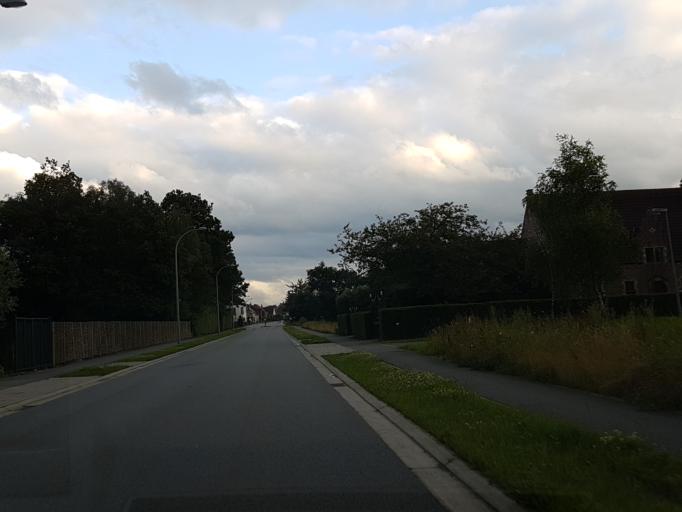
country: BE
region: Flanders
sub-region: Provincie Oost-Vlaanderen
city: Buggenhout
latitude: 50.9911
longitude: 4.2136
